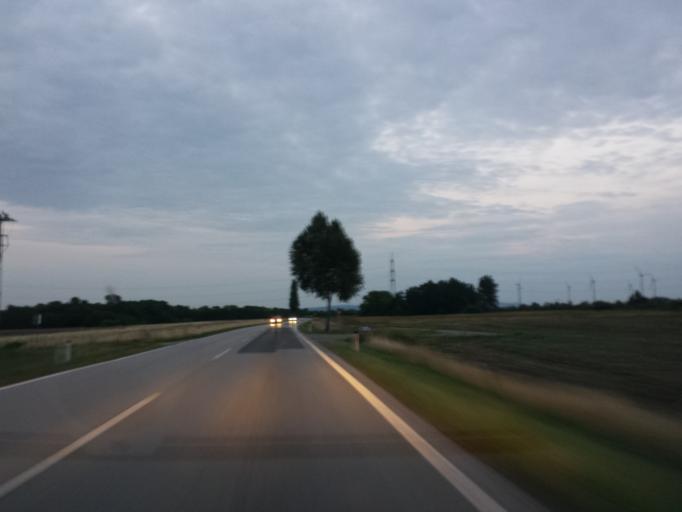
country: AT
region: Lower Austria
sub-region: Politischer Bezirk Baden
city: Oberwaltersdorf
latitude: 47.9651
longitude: 16.3459
